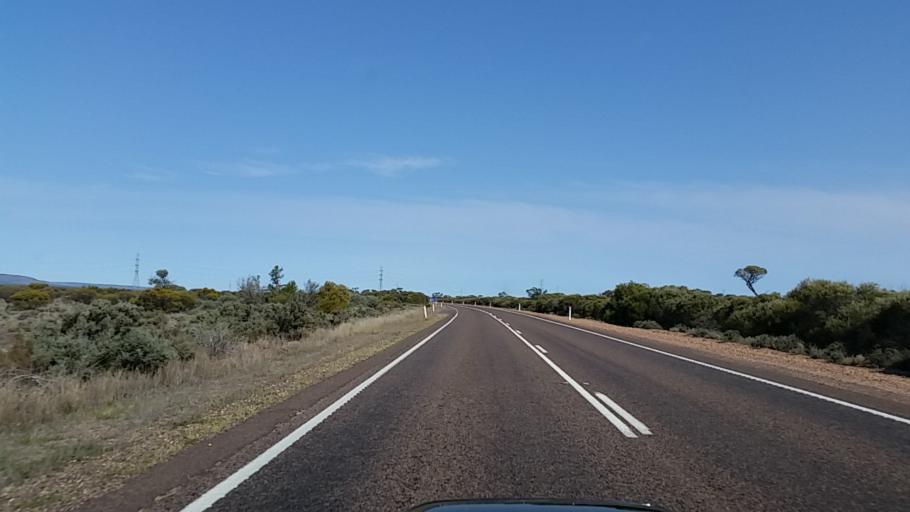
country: AU
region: South Australia
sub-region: Whyalla
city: Whyalla
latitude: -32.7232
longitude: 137.5087
